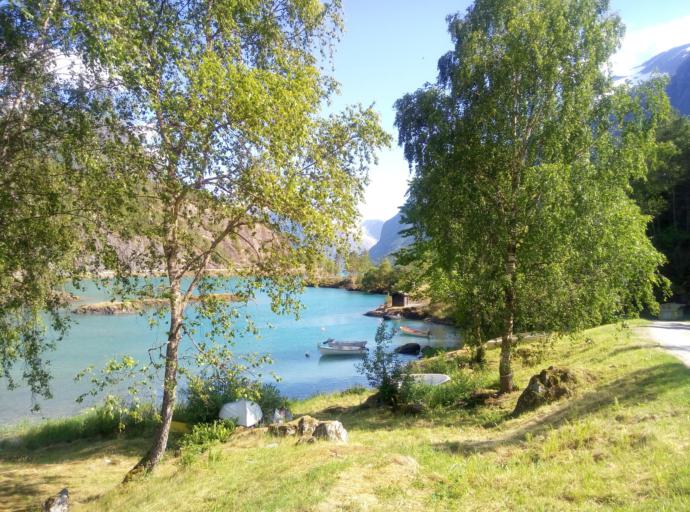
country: NO
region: Sogn og Fjordane
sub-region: Stryn
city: Stryn
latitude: 61.8597
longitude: 6.8884
